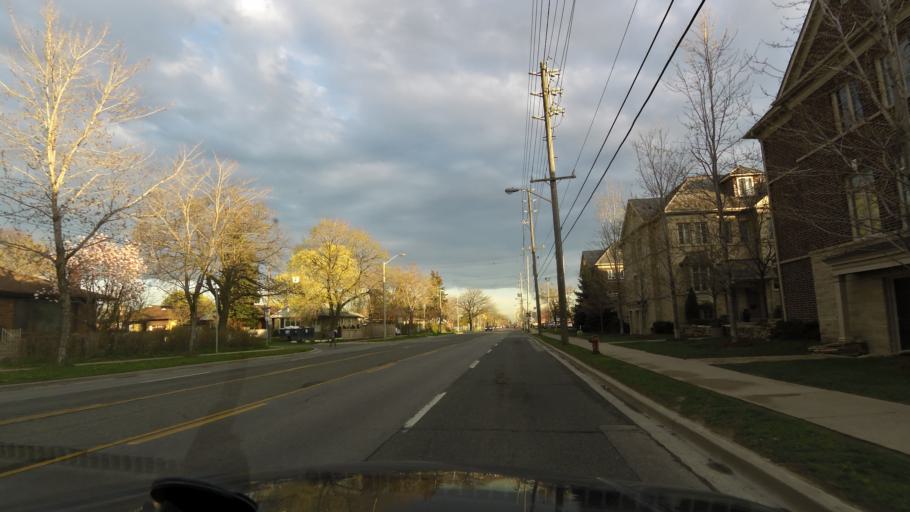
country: CA
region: Ontario
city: Etobicoke
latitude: 43.6376
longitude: -79.5206
